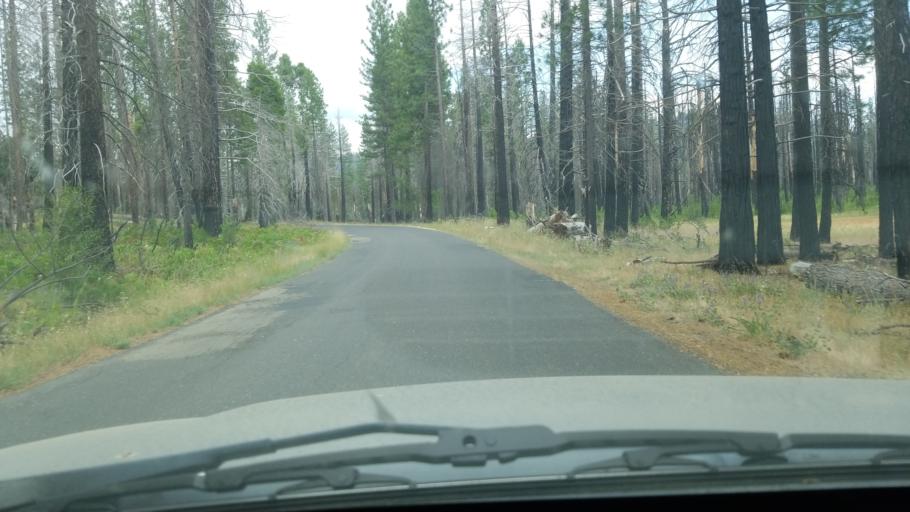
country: US
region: California
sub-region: Mariposa County
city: Yosemite Valley
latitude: 37.8393
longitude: -119.8521
